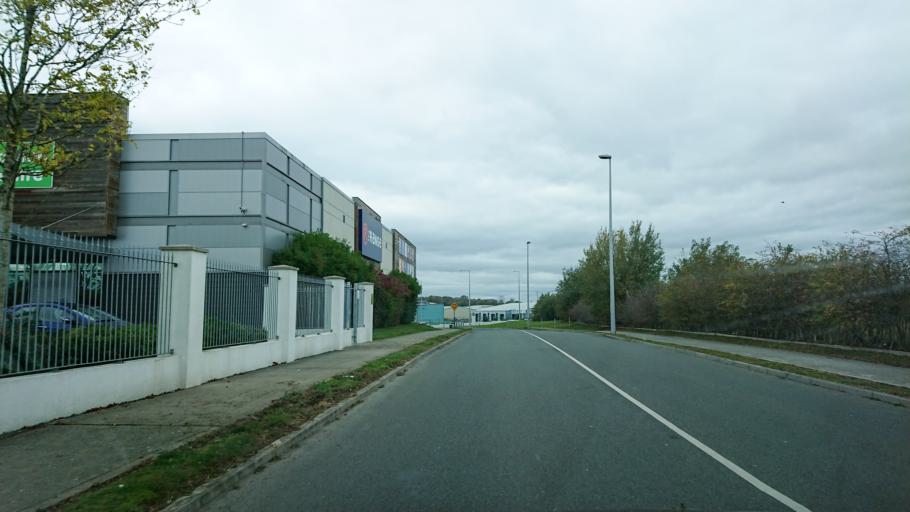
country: IE
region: Munster
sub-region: Waterford
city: Waterford
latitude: 52.2322
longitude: -7.1404
